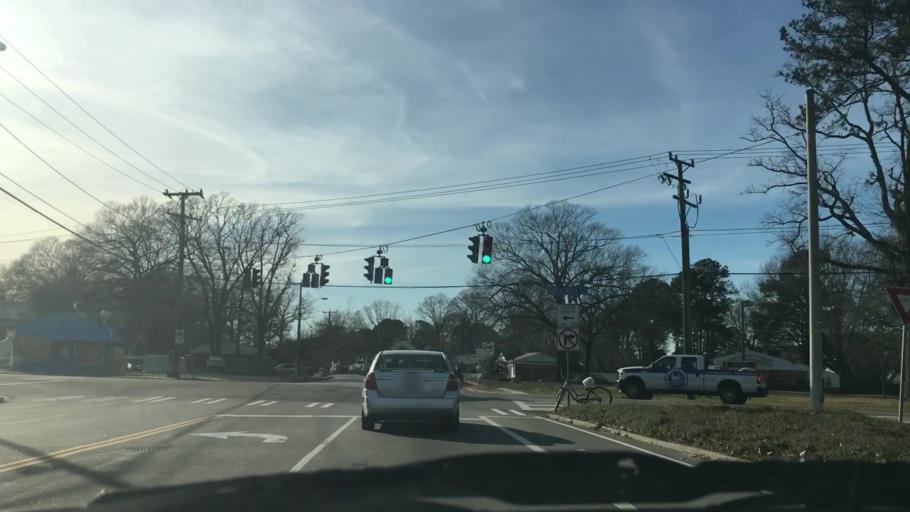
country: US
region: Virginia
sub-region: City of Norfolk
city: Norfolk
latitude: 36.8792
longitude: -76.2265
